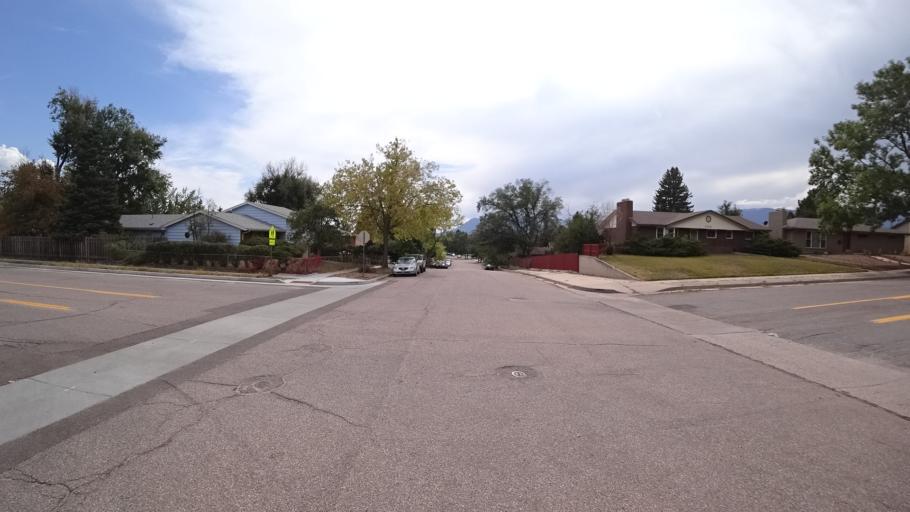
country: US
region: Colorado
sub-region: El Paso County
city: Colorado Springs
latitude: 38.8633
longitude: -104.7841
